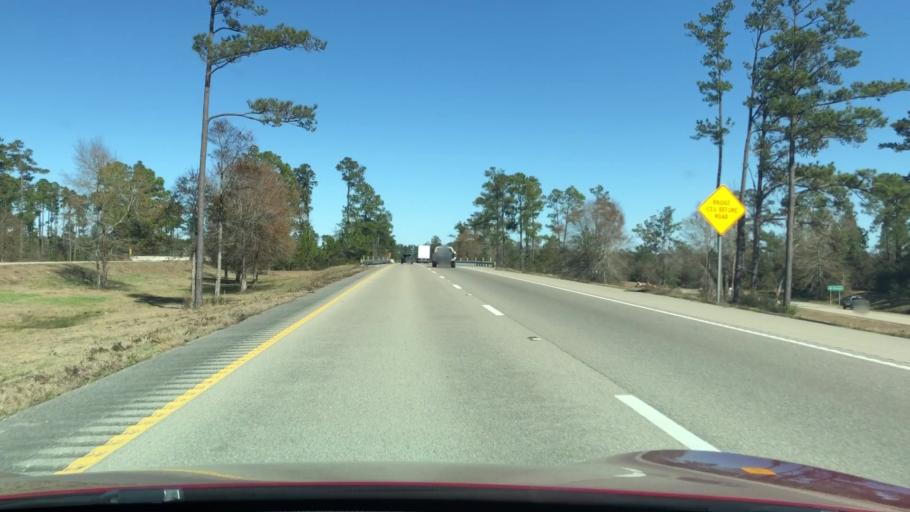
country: US
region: Mississippi
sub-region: Pearl River County
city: Poplarville
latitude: 30.7165
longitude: -89.5551
